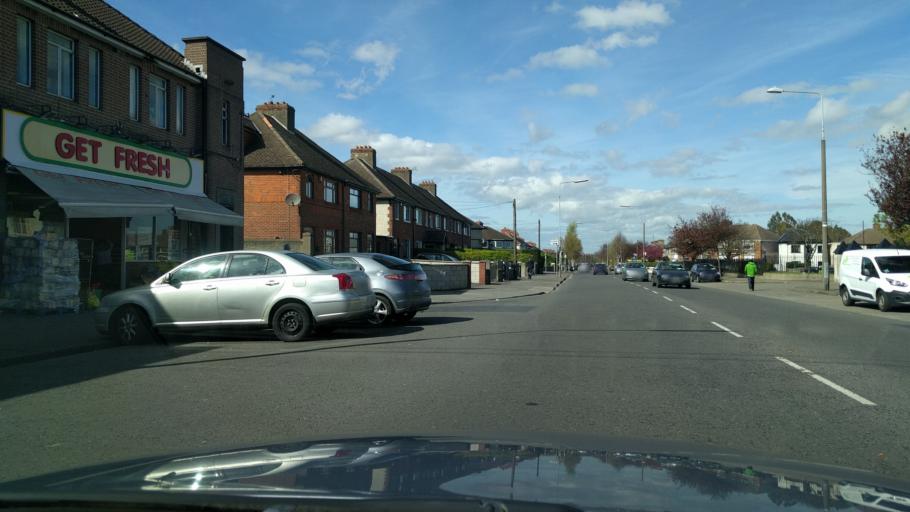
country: IE
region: Leinster
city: Rialto
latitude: 53.3247
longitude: -6.2961
